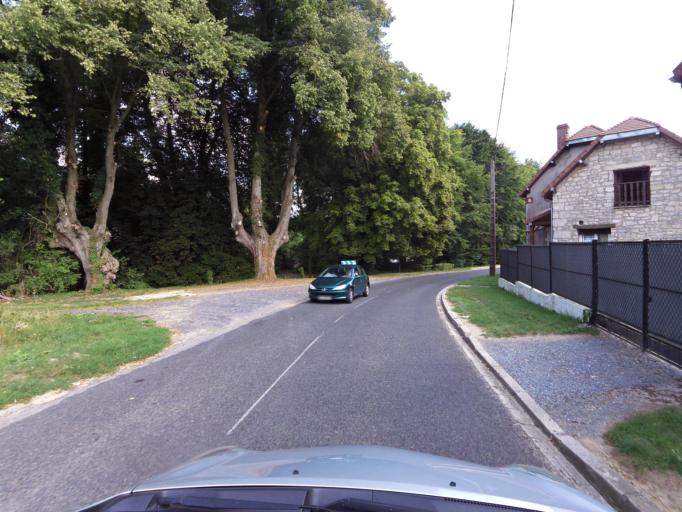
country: FR
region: Picardie
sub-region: Departement de l'Aisne
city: Bruyeres-et-Montberault
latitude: 49.4747
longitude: 3.6527
